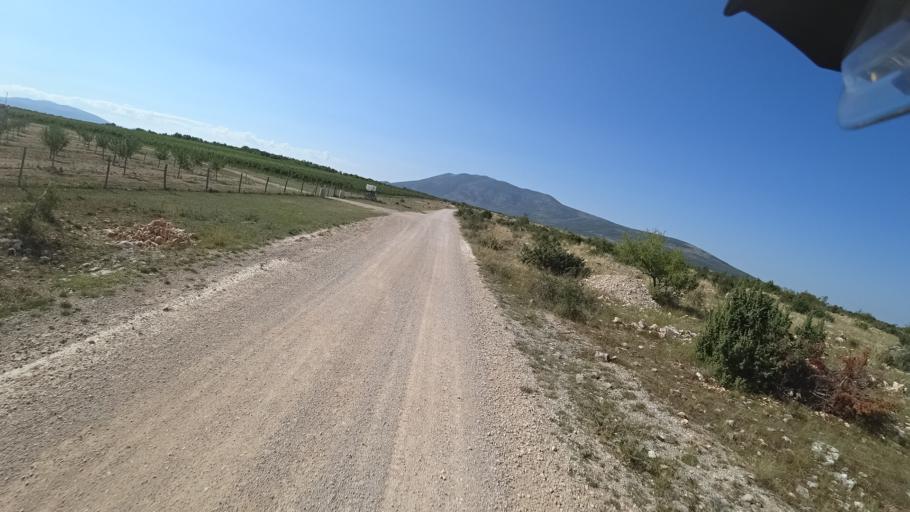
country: HR
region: Sibensko-Kniniska
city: Knin
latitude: 43.9923
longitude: 16.1929
